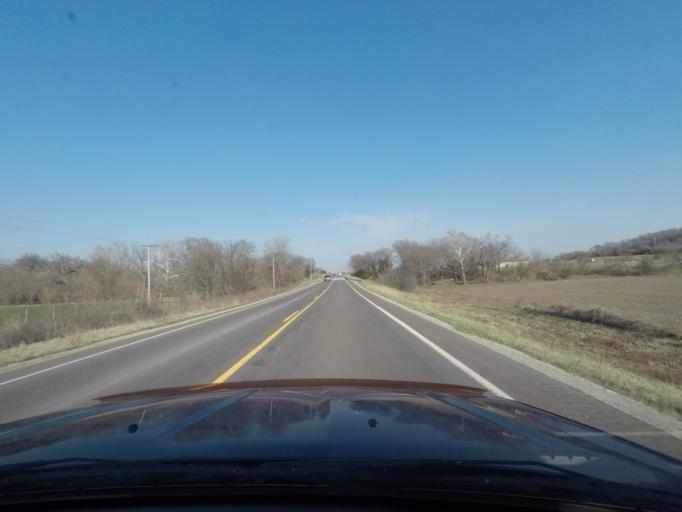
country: US
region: Kansas
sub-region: Douglas County
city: Lawrence
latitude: 39.0006
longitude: -95.2956
